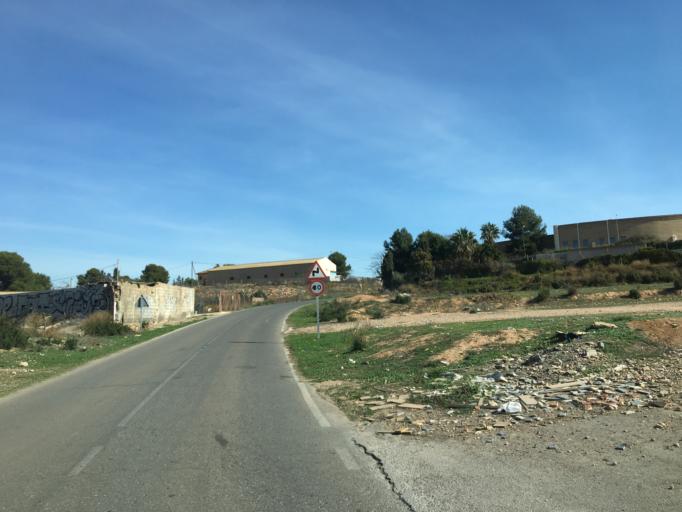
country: ES
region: Murcia
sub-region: Murcia
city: Cartagena
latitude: 37.6361
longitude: -1.0190
